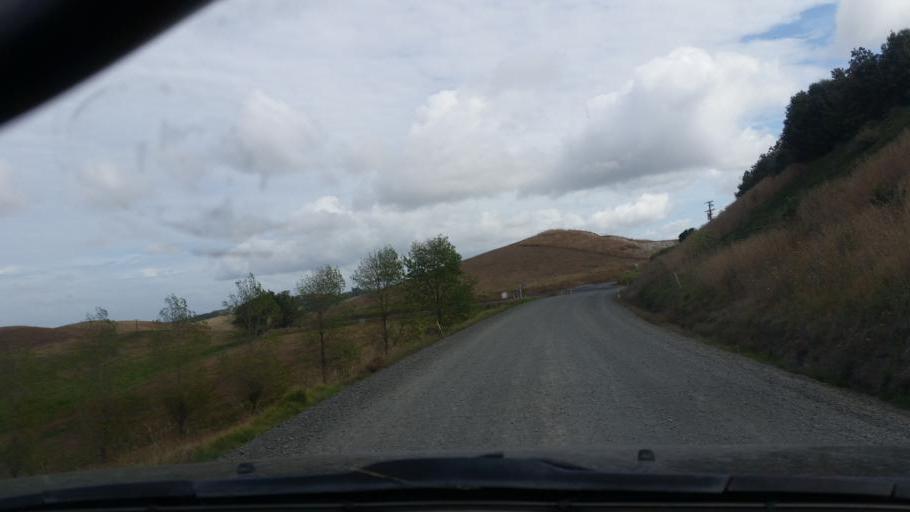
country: NZ
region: Northland
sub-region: Kaipara District
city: Dargaville
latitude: -35.9760
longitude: 173.9518
